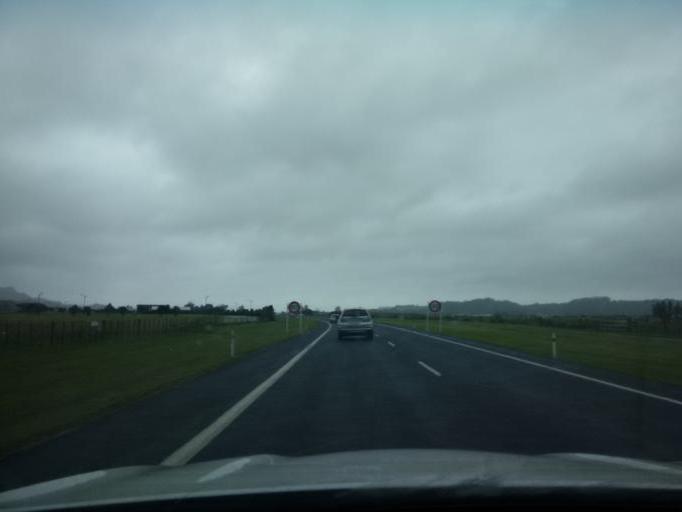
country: NZ
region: Waikato
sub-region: Thames-Coromandel District
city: Whitianga
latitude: -36.8323
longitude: 175.6796
